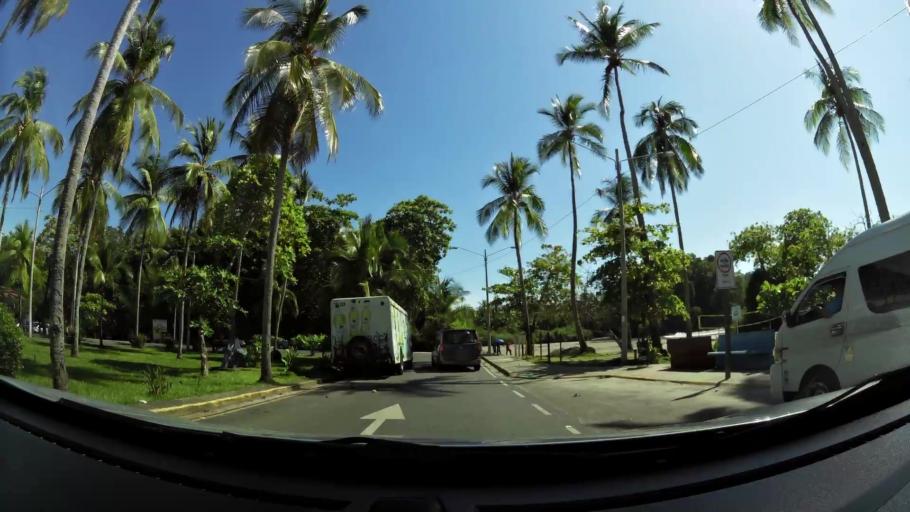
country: CR
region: Puntarenas
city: Quepos
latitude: 9.3896
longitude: -84.1474
